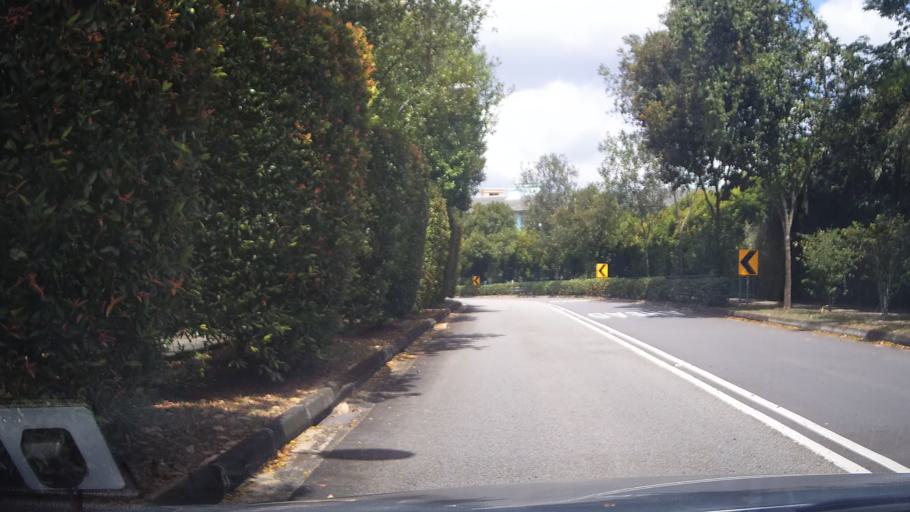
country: SG
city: Singapore
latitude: 1.3221
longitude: 103.7591
